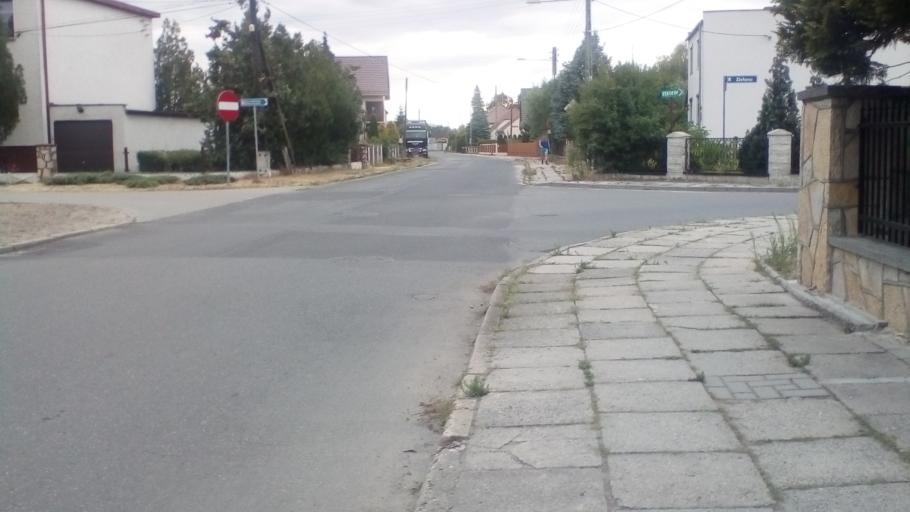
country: PL
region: Opole Voivodeship
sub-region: Powiat opolski
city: Tarnow Opolski
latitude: 50.5802
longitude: 18.0806
